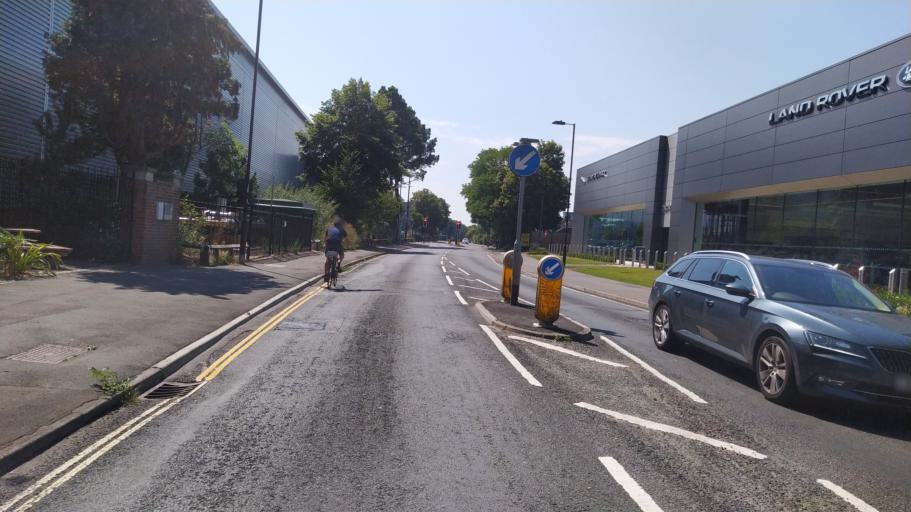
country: GB
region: England
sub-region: Hampshire
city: Eastleigh
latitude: 50.9454
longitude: -1.3686
